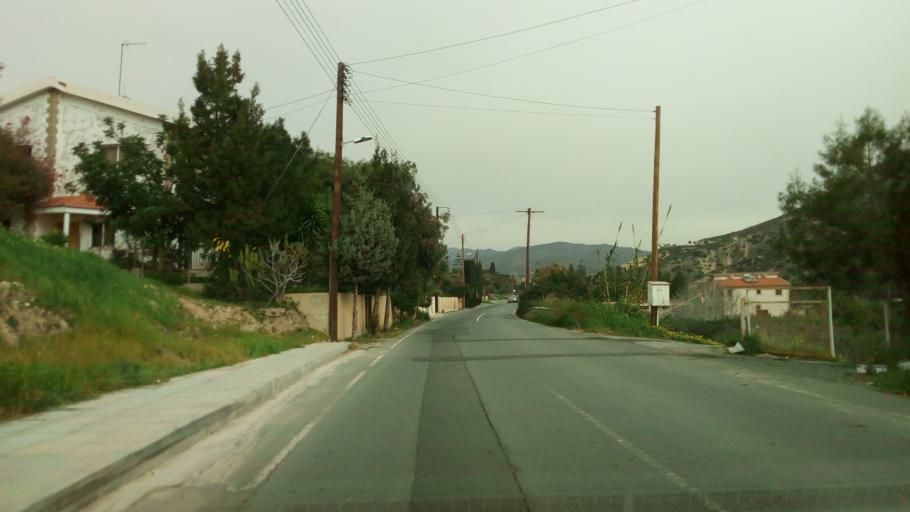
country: CY
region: Limassol
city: Mouttagiaka
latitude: 34.7345
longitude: 33.0828
